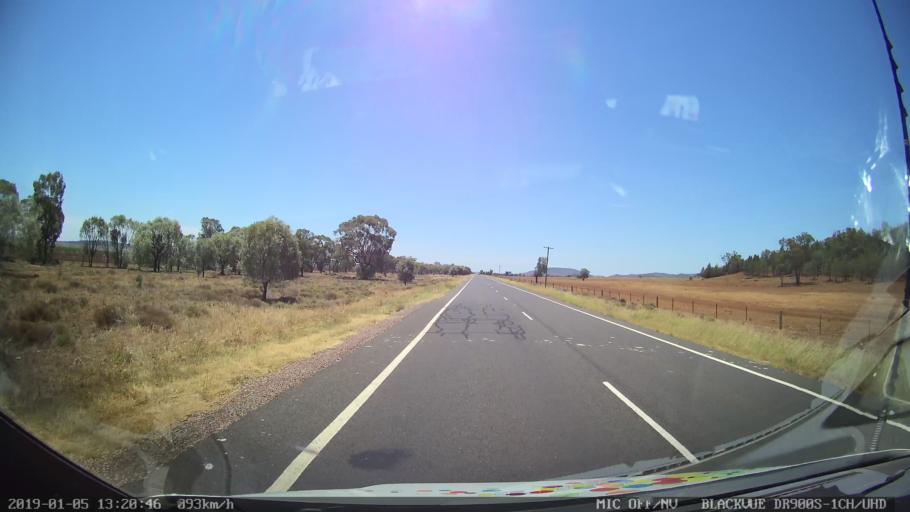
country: AU
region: New South Wales
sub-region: Gunnedah
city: Gunnedah
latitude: -31.0997
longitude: 149.9400
